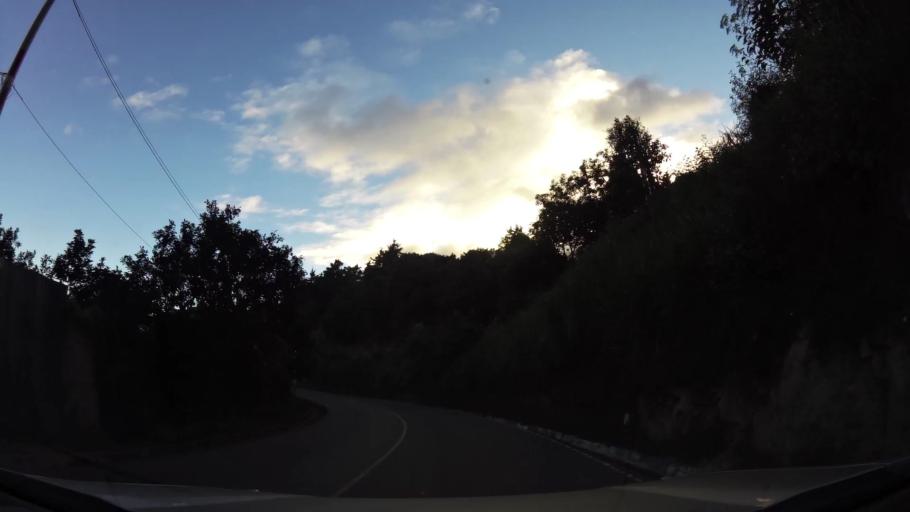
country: GT
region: Quiche
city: Chichicastenango
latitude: 14.9350
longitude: -91.1095
